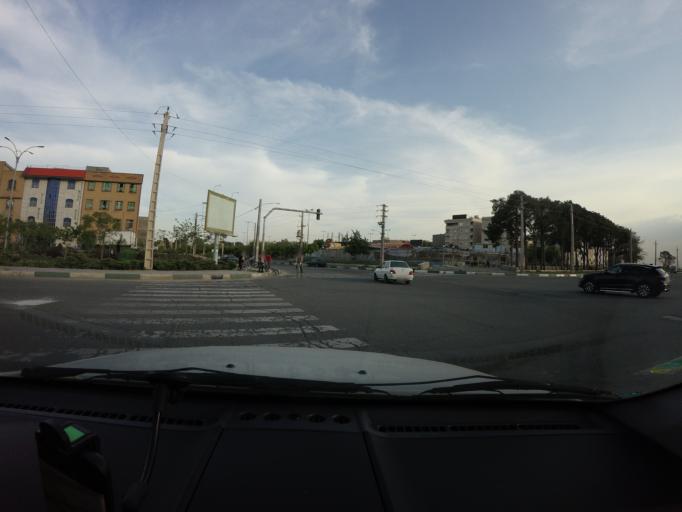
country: IR
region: Tehran
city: Eslamshahr
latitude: 35.5303
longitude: 51.2130
